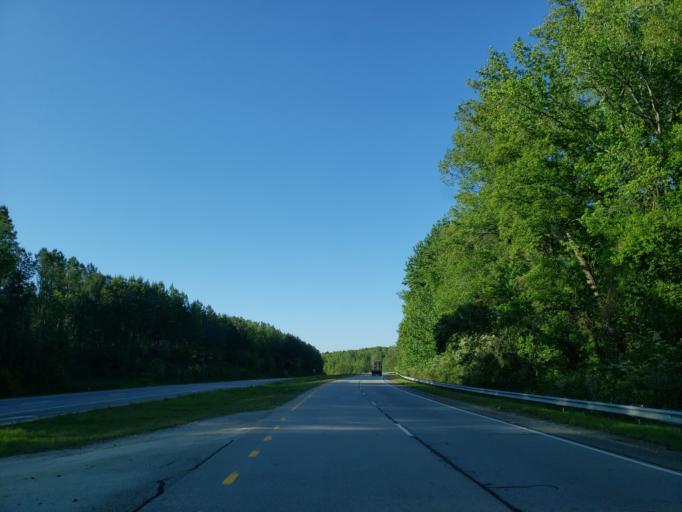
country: US
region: Georgia
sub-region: Haralson County
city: Buchanan
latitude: 33.8422
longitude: -85.2089
